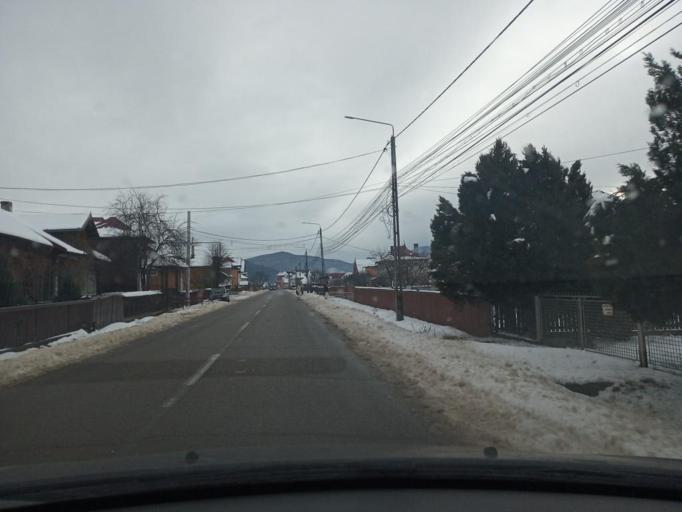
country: RO
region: Suceava
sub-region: Comuna Manastirea Humorului
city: Manastirea Humorului
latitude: 47.5791
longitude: 25.8735
